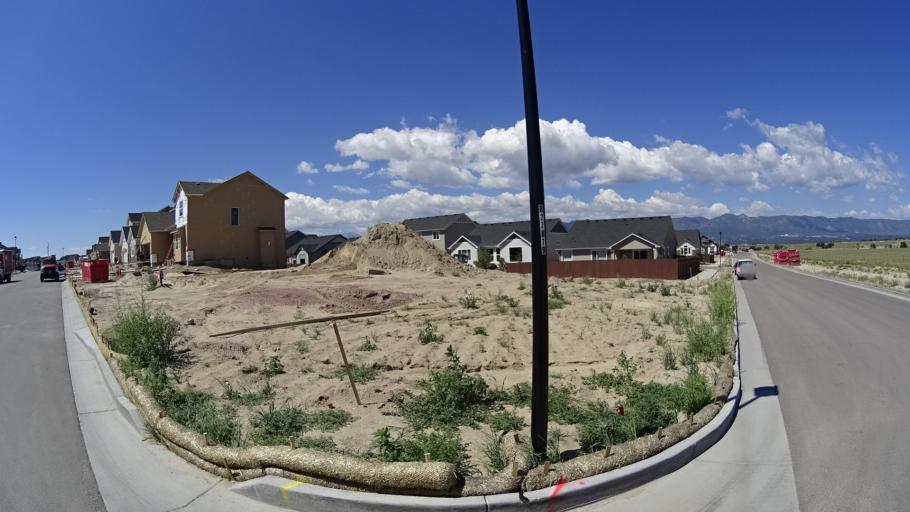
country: US
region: Colorado
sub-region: El Paso County
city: Black Forest
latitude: 38.9946
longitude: -104.7703
